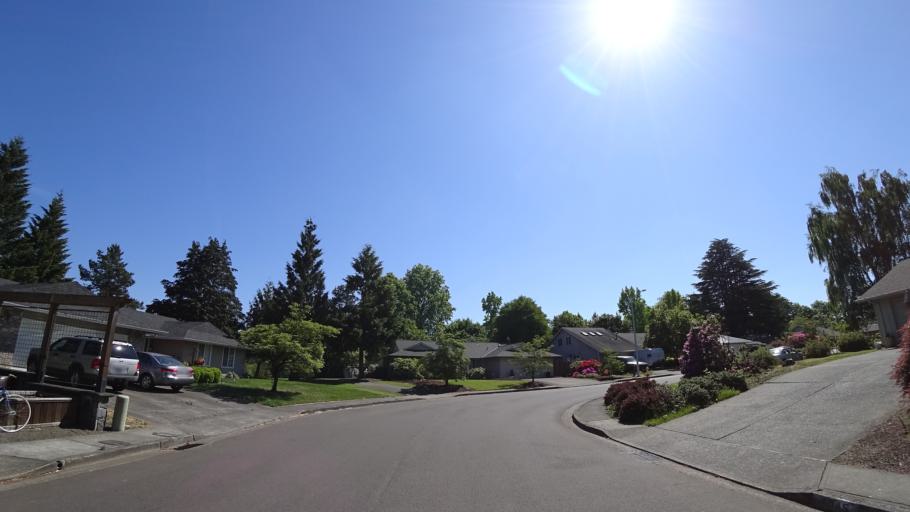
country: US
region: Oregon
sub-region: Washington County
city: Beaverton
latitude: 45.4545
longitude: -122.7975
